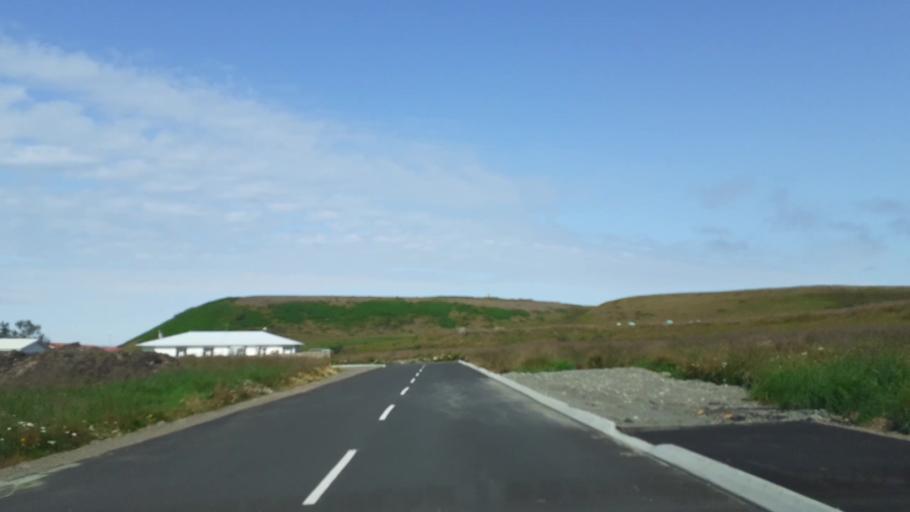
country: IS
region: Northwest
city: Saudarkrokur
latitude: 65.6640
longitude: -20.2841
